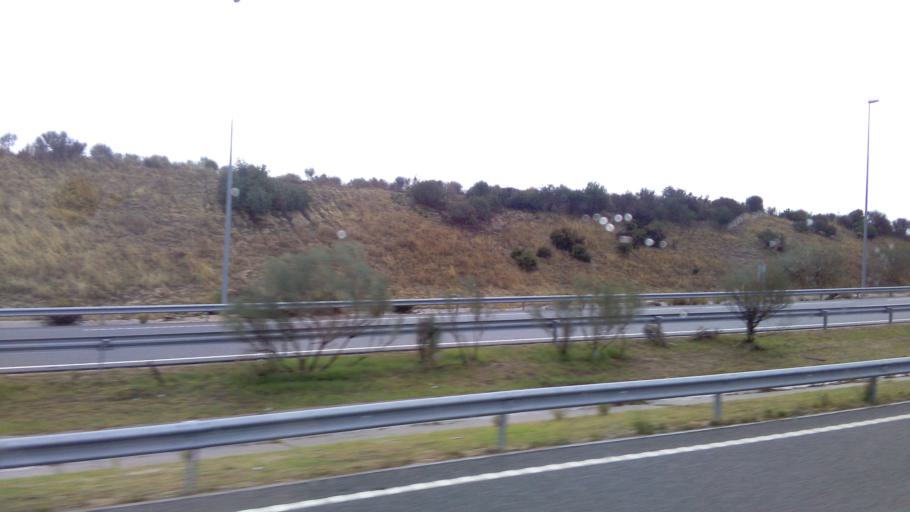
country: ES
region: Madrid
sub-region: Provincia de Madrid
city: Alcorcon
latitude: 40.3338
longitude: -3.8112
